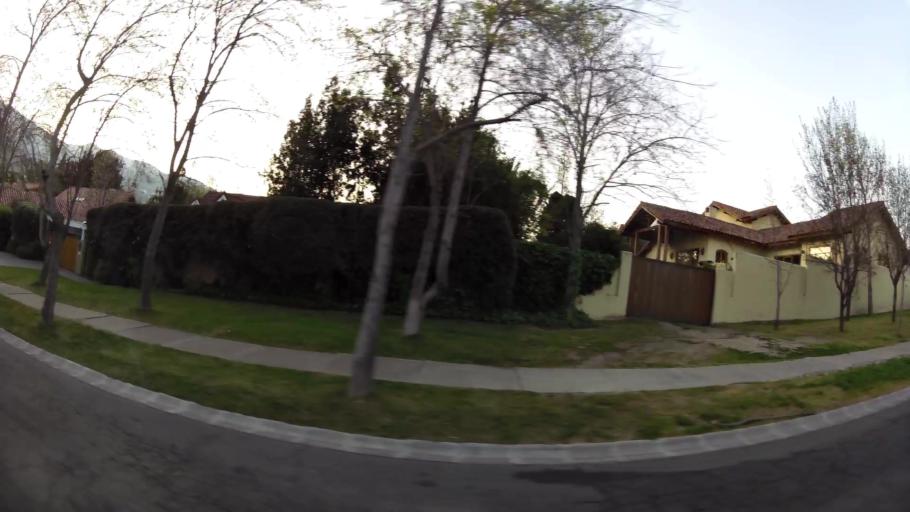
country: CL
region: Santiago Metropolitan
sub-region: Provincia de Chacabuco
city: Chicureo Abajo
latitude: -33.3433
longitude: -70.5481
